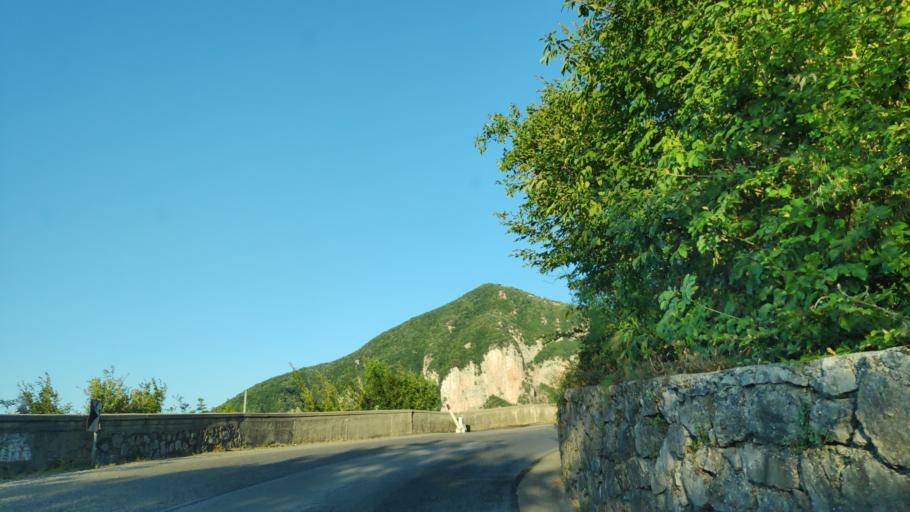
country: IT
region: Campania
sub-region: Provincia di Salerno
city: Corbara
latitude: 40.7250
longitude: 14.6055
